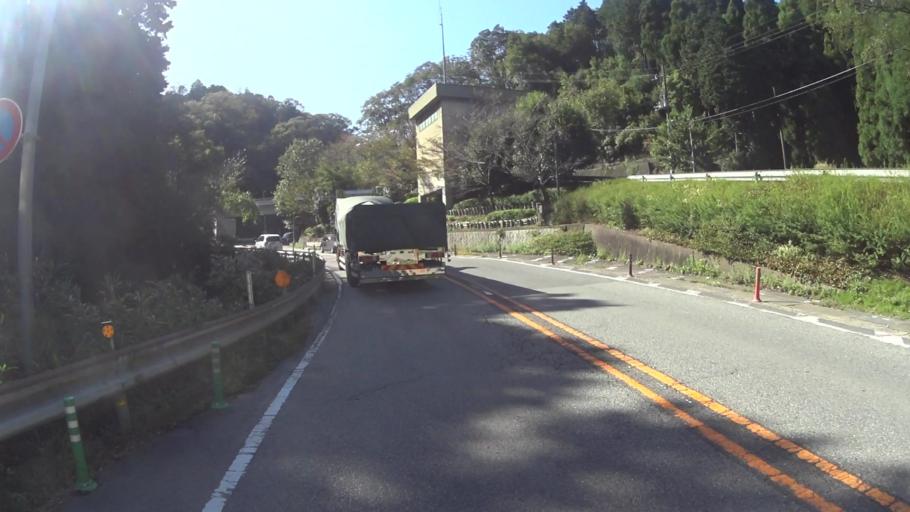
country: JP
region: Kyoto
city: Kameoka
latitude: 34.9854
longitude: 135.6391
